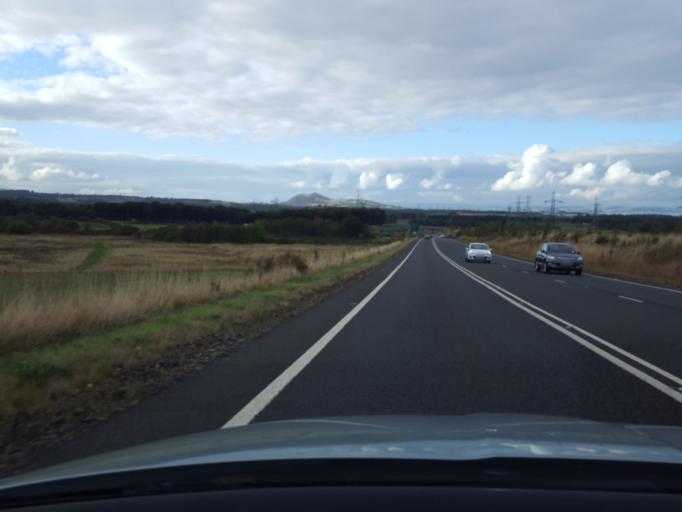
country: GB
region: Scotland
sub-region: Midlothian
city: Dalkeith
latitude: 55.9056
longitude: -3.0348
